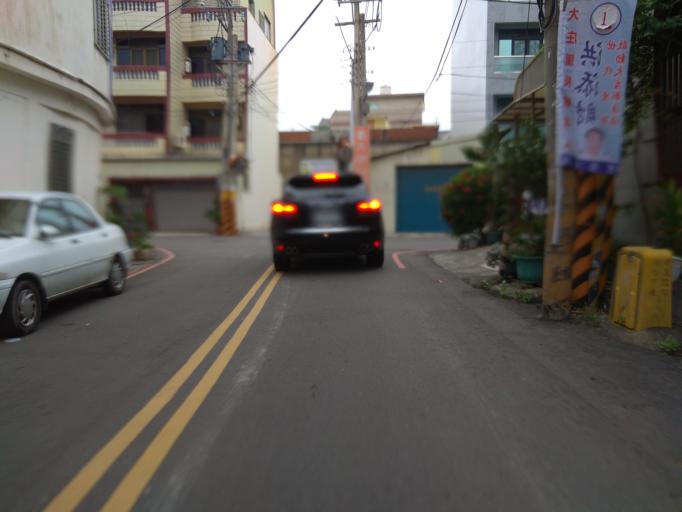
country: TW
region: Taiwan
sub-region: Hsinchu
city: Hsinchu
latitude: 24.7935
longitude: 120.9220
